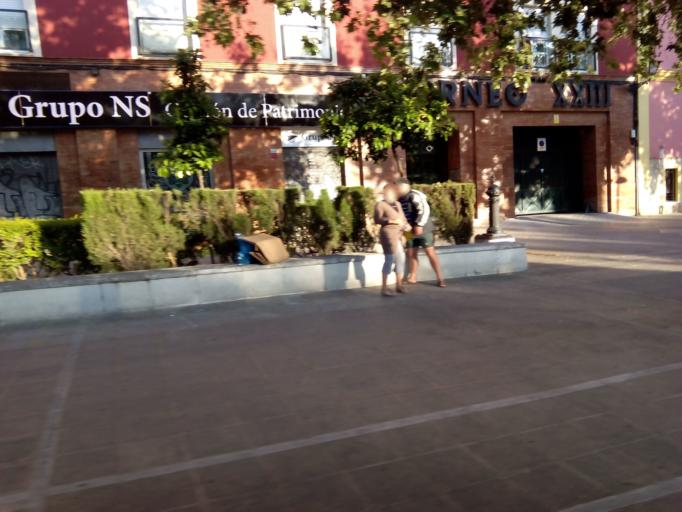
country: ES
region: Andalusia
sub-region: Provincia de Sevilla
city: Sevilla
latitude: 37.4018
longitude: -5.9973
